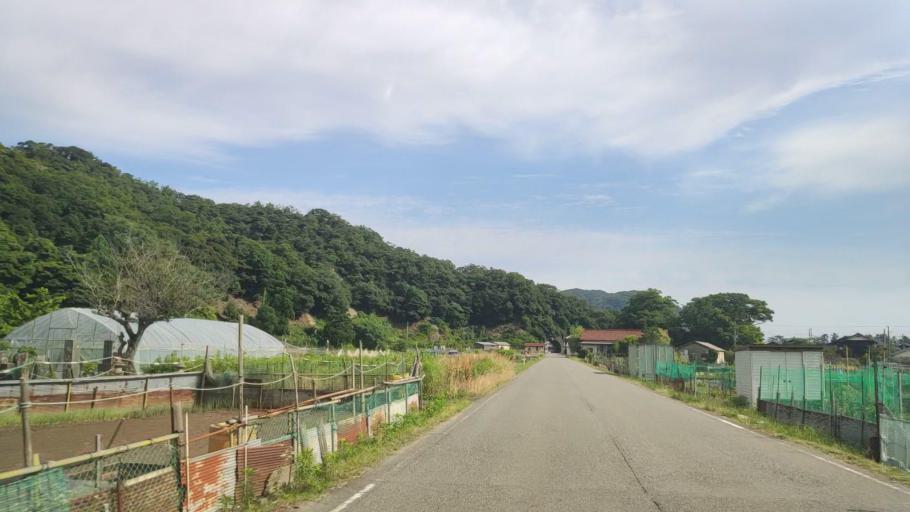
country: JP
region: Hyogo
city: Toyooka
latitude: 35.6368
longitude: 134.8364
